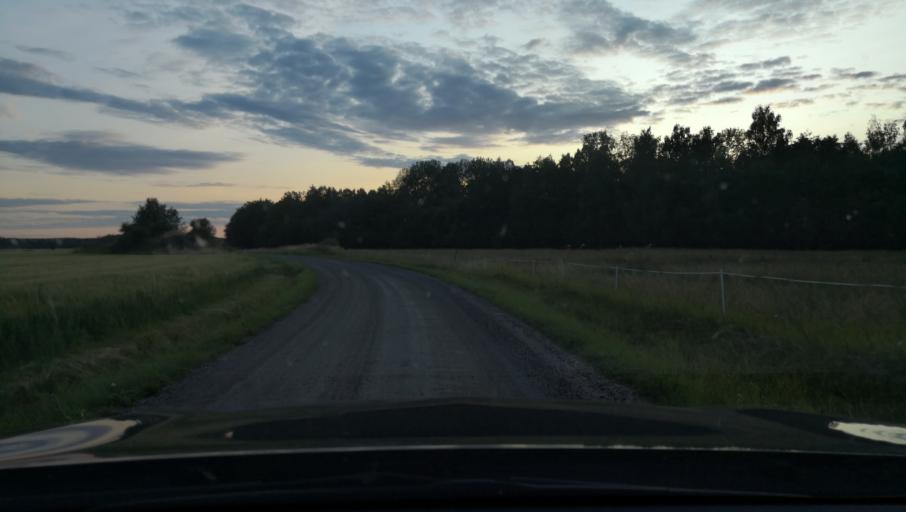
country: SE
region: Uppsala
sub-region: Osthammars Kommun
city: Bjorklinge
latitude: 60.0550
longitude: 17.6021
